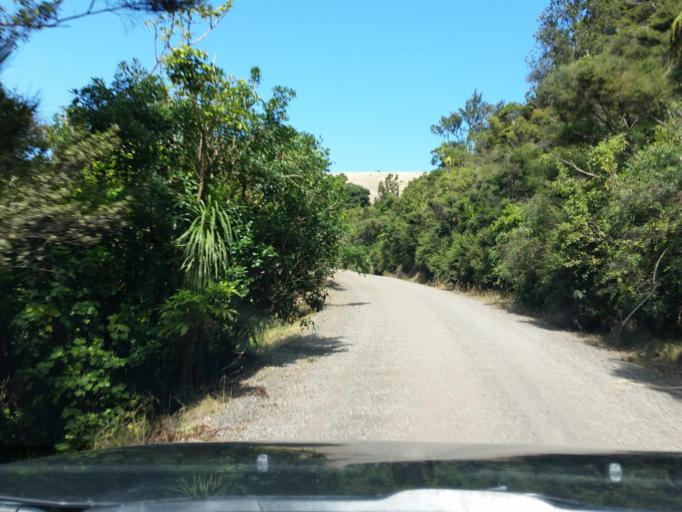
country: NZ
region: Northland
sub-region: Kaipara District
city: Dargaville
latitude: -35.7144
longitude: 173.5501
